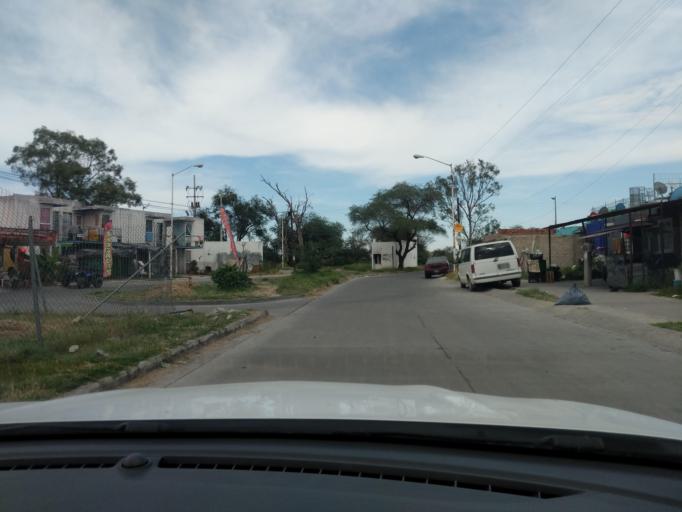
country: MX
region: Jalisco
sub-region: El Salto
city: Galaxia Bonito Jalisco
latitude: 20.5097
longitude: -103.1906
